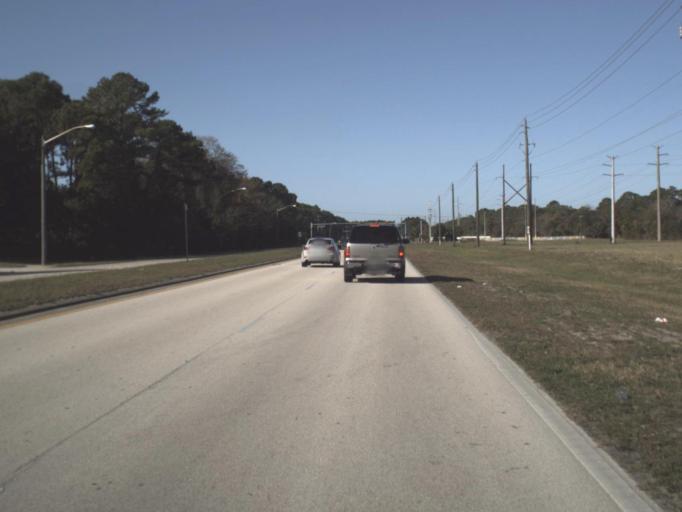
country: US
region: Florida
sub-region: Volusia County
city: Holly Hill
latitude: 29.2150
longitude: -81.0667
